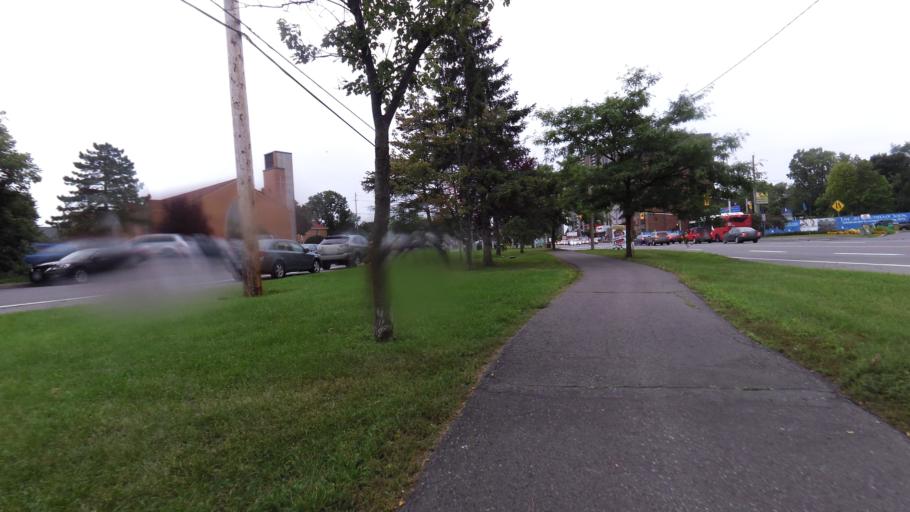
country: CA
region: Ontario
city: Ottawa
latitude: 45.3781
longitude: -75.7741
